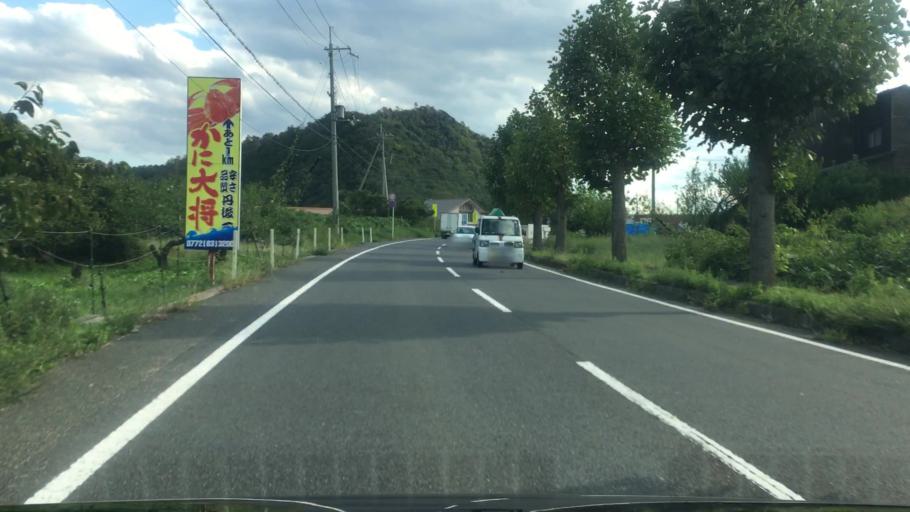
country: JP
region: Hyogo
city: Toyooka
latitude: 35.6236
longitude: 134.9285
